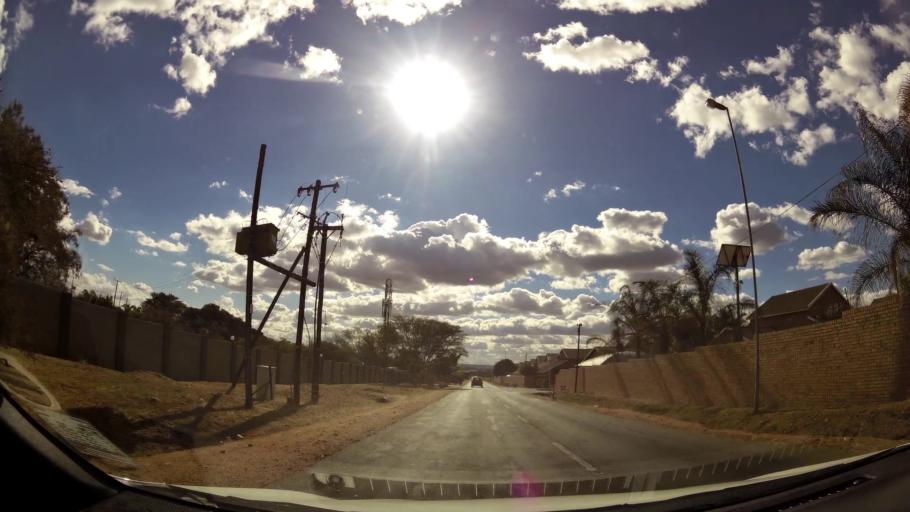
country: ZA
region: Limpopo
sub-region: Capricorn District Municipality
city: Polokwane
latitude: -23.8814
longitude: 29.4829
